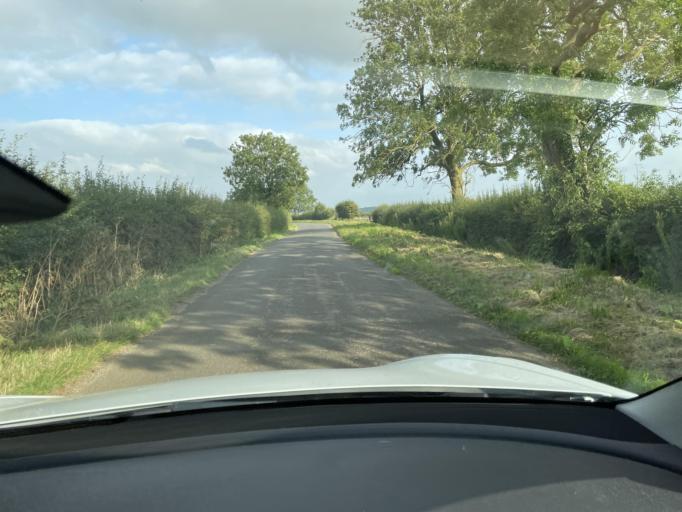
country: GB
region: England
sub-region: Northamptonshire
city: Long Buckby
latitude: 52.4195
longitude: -1.0388
